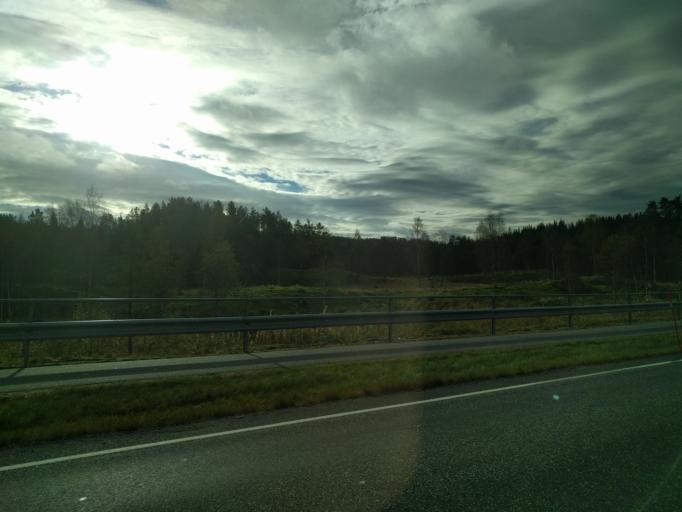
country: NO
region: Vest-Agder
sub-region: Kristiansand
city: Strai
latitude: 58.2858
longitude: 7.8429
